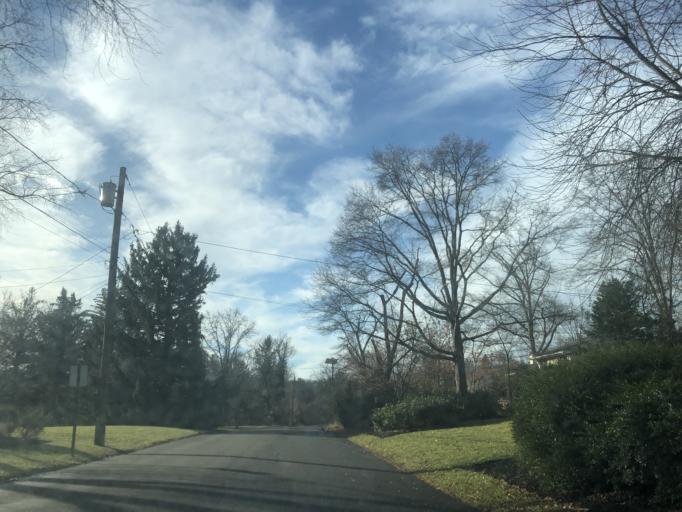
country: US
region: New Jersey
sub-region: Somerset County
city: Kingston
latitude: 40.3665
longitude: -74.6378
